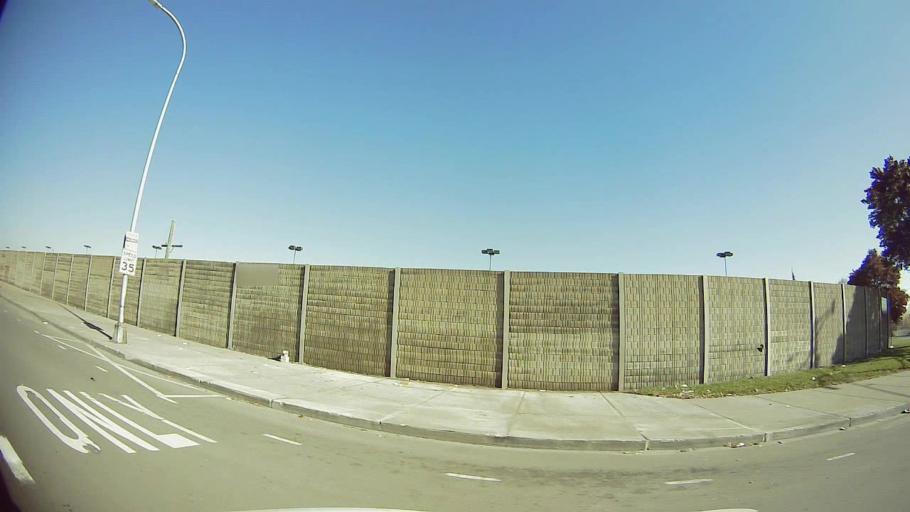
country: US
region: Michigan
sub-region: Wayne County
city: Dearborn
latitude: 42.3449
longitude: -83.1305
